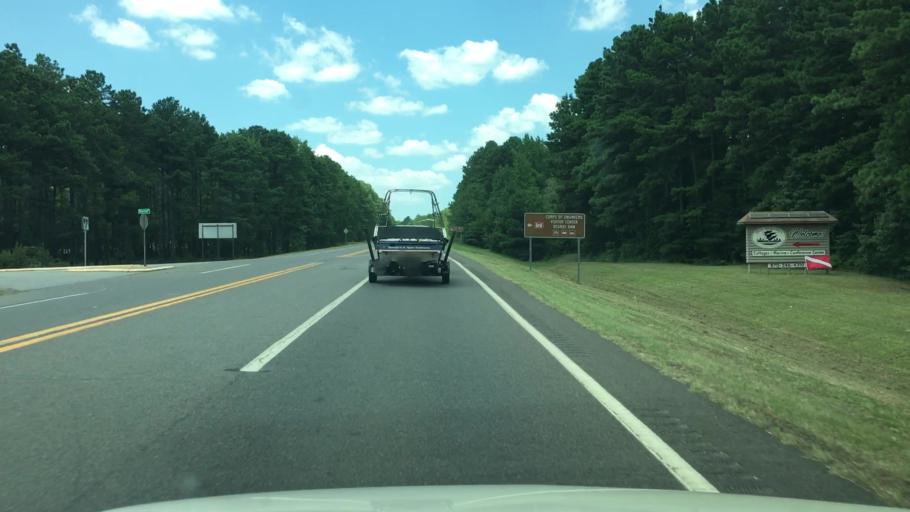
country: US
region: Arkansas
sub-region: Clark County
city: Arkadelphia
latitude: 34.2196
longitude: -93.0865
